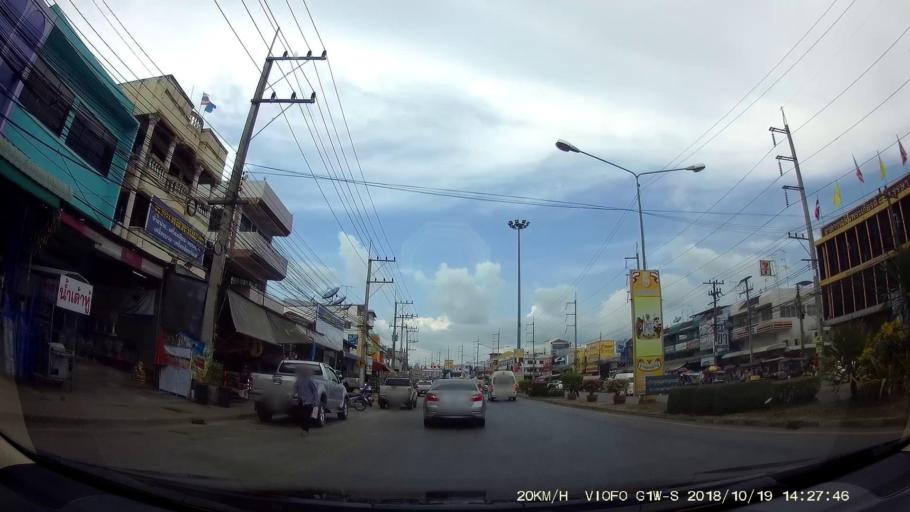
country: TH
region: Chaiyaphum
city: Kaeng Khro
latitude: 16.1125
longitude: 102.2575
